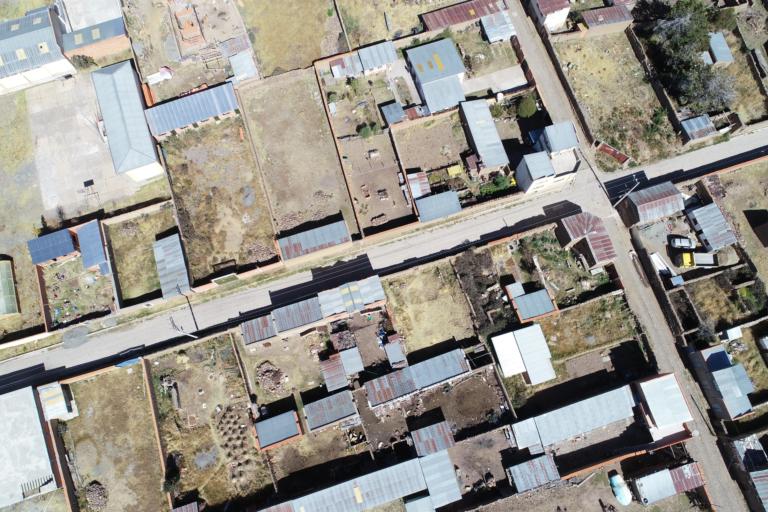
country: BO
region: La Paz
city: Achacachi
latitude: -15.8978
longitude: -68.9039
